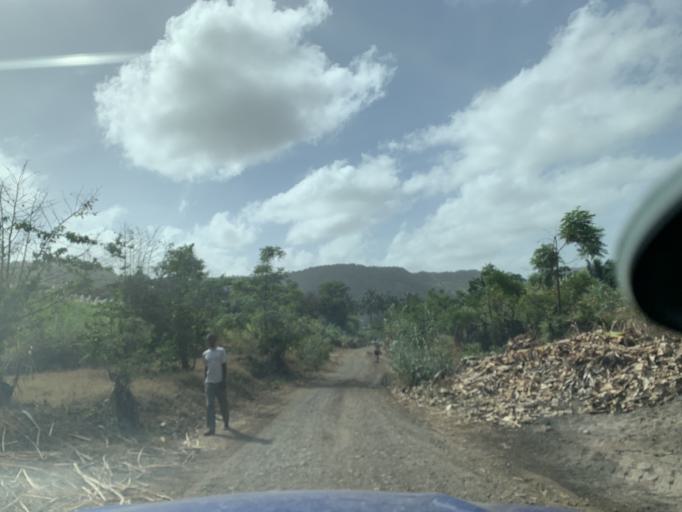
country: CV
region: Santa Cruz
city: Pedra Badejo
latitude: 15.1226
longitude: -23.5467
